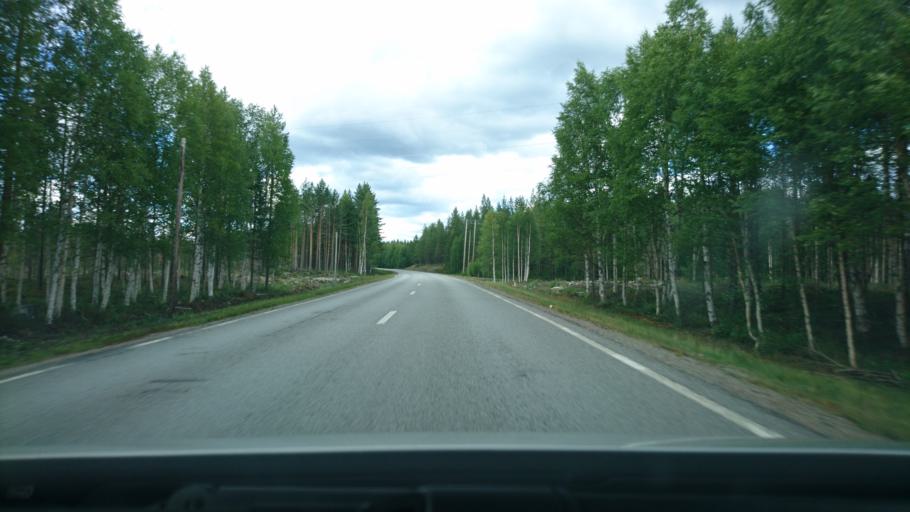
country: SE
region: Vaesterbotten
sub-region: Asele Kommun
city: Asele
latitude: 63.8752
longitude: 17.2008
